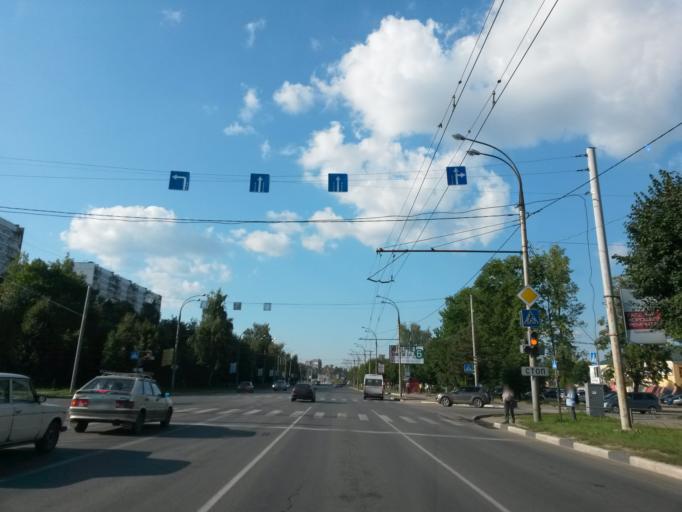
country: RU
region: Ivanovo
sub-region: Gorod Ivanovo
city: Ivanovo
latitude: 56.9610
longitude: 40.9740
